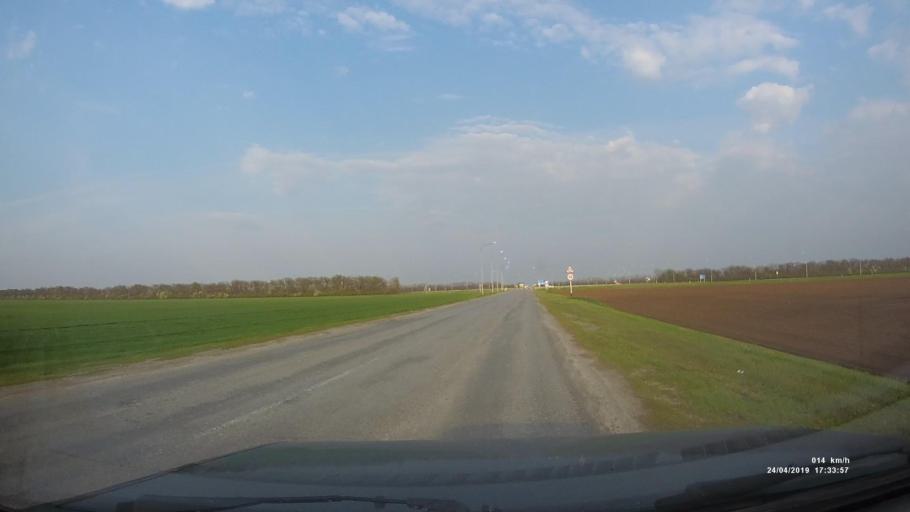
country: RU
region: Rostov
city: Tselina
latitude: 46.5269
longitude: 41.0763
